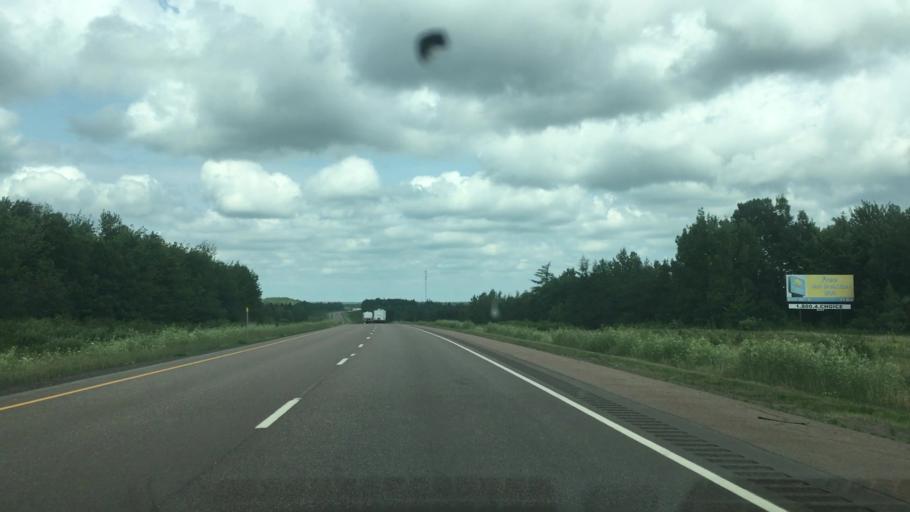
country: CA
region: New Brunswick
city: Dieppe
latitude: 46.0647
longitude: -64.5884
